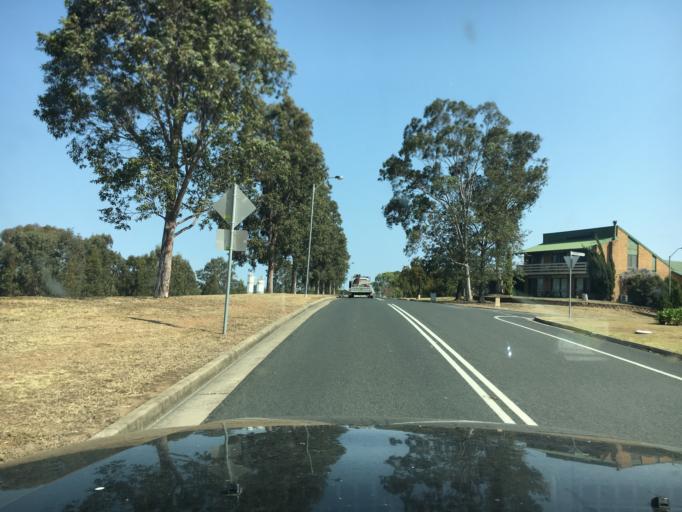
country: AU
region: New South Wales
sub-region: Singleton
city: Singleton
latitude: -32.5598
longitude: 151.1596
